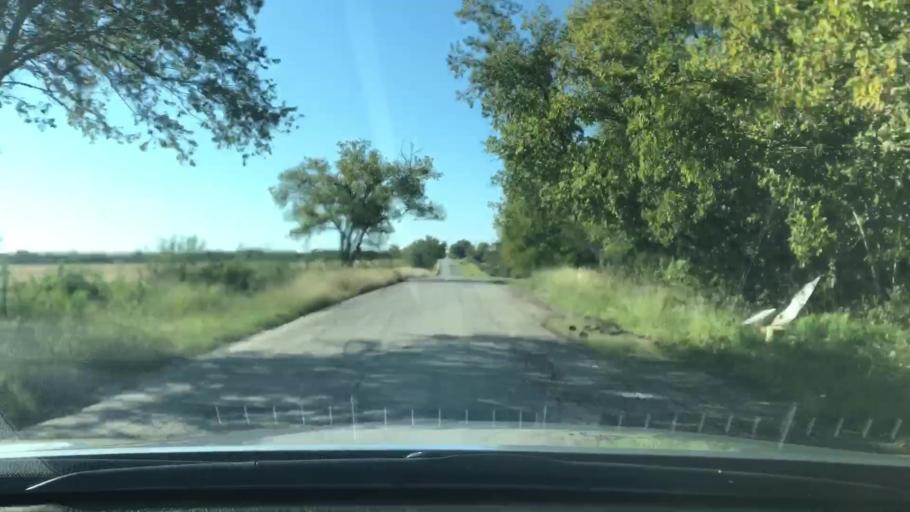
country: US
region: Texas
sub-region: Bexar County
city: Converse
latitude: 29.4662
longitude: -98.2955
